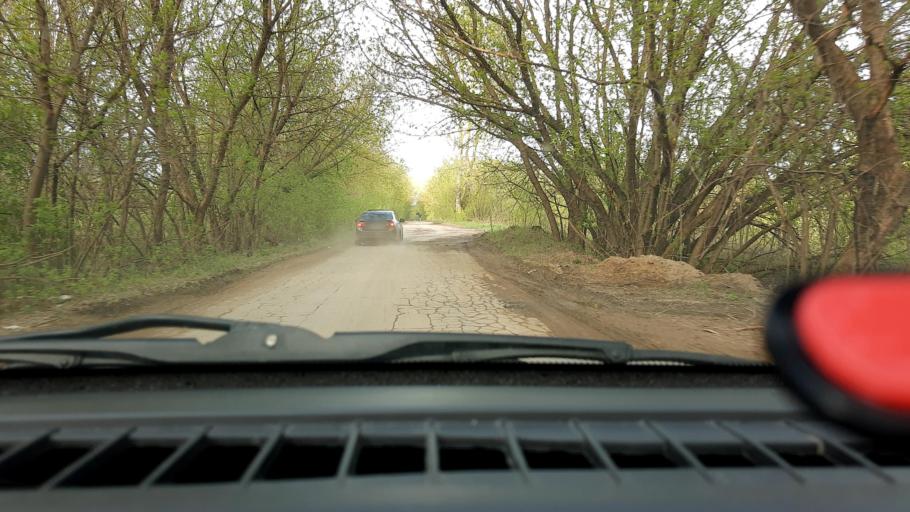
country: RU
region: Nizjnij Novgorod
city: Neklyudovo
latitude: 56.3913
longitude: 43.8440
